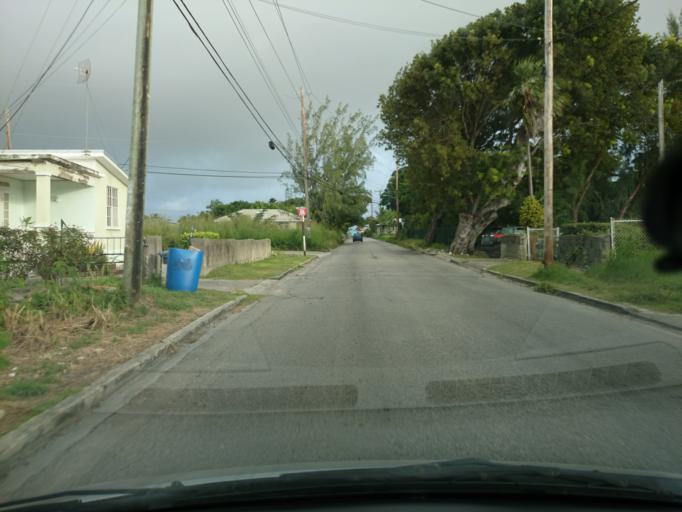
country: BB
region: Christ Church
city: Oistins
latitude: 13.0600
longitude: -59.5347
